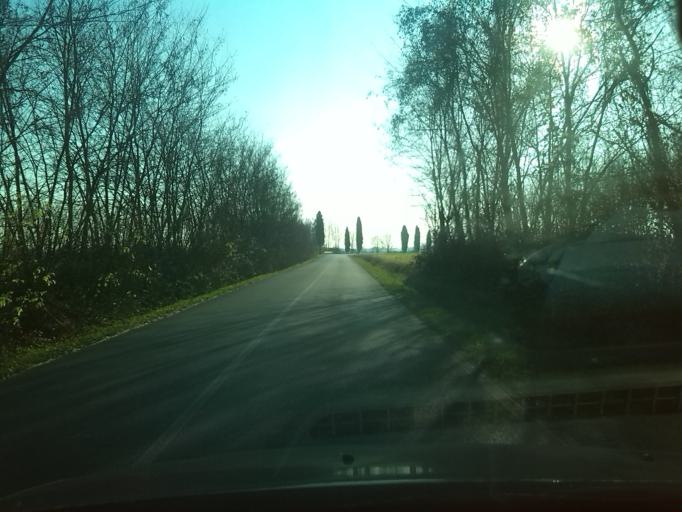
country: IT
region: Friuli Venezia Giulia
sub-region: Provincia di Udine
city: Santa Maria la Longa
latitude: 45.9456
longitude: 13.3015
